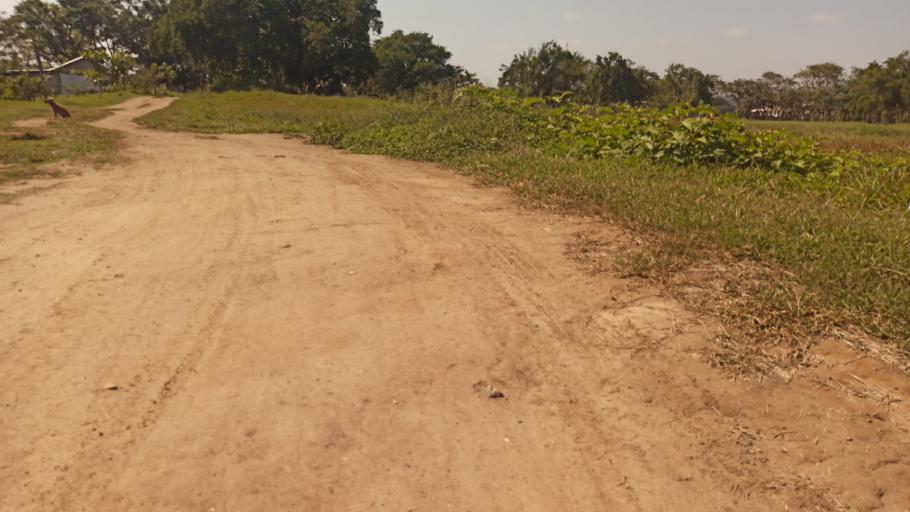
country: MX
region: Puebla
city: San Jose Acateno
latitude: 20.1626
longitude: -97.1659
